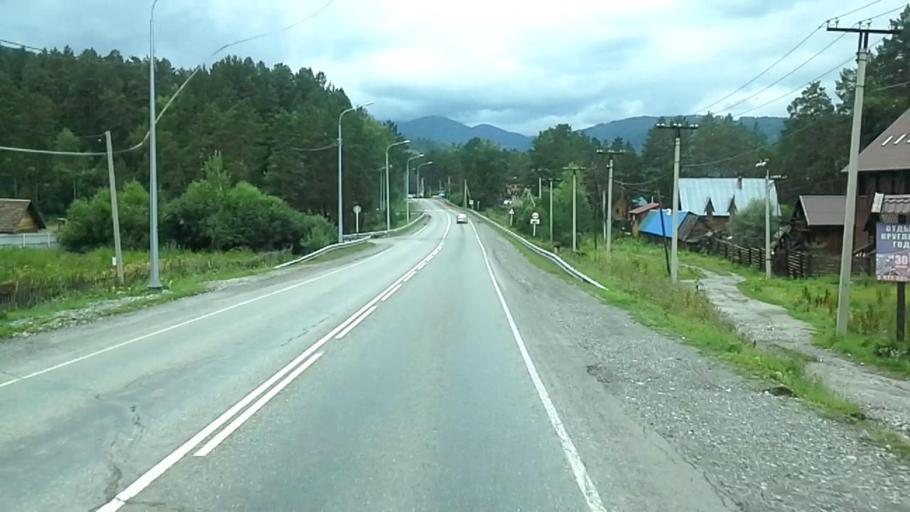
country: RU
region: Altay
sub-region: Mayminskiy Rayon
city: Manzherok
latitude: 51.8193
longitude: 85.7830
